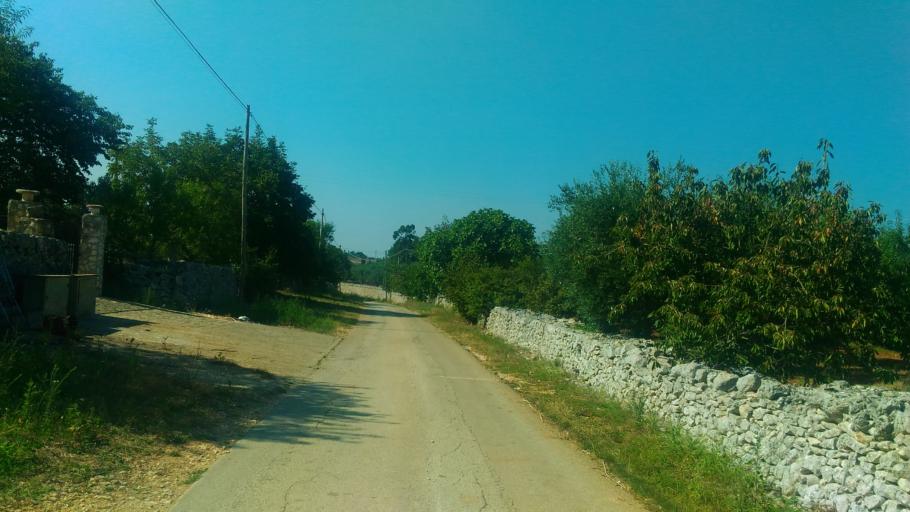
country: IT
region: Apulia
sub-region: Provincia di Bari
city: Noci
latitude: 40.8193
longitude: 17.1761
